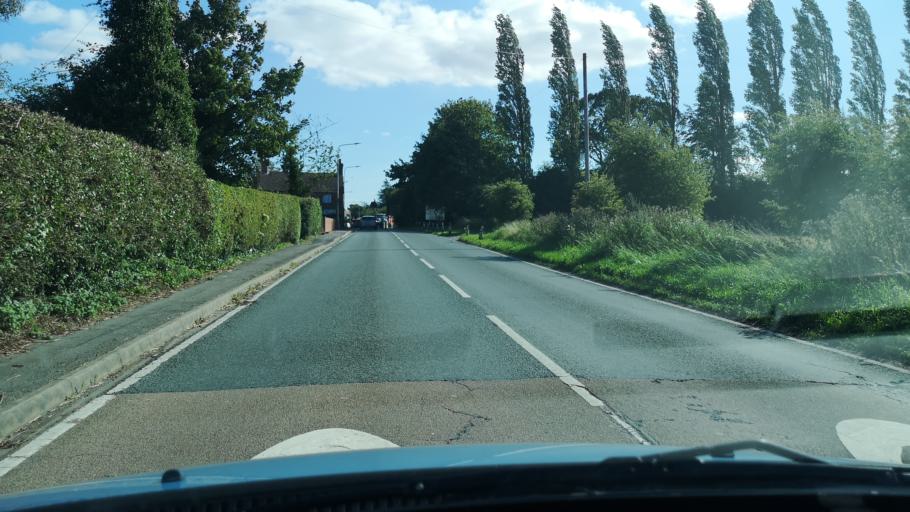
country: GB
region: England
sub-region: North Lincolnshire
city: Belton
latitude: 53.5582
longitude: -0.8170
